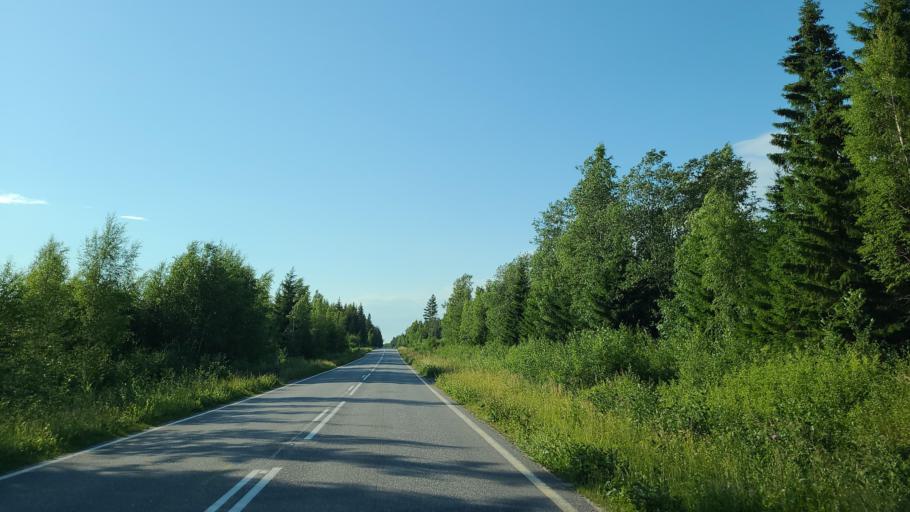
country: FI
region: Ostrobothnia
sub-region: Vaasa
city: Replot
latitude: 63.2420
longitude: 21.3837
